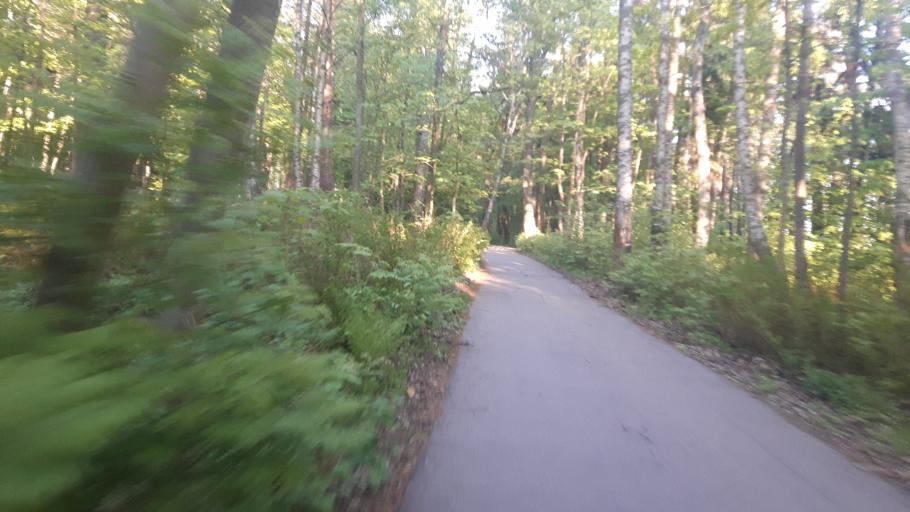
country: RU
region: Leningrad
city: Roshchino
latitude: 60.1941
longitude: 29.6254
